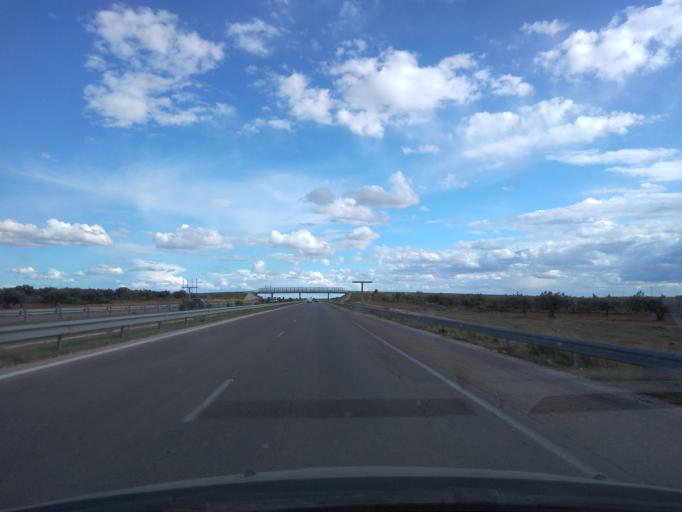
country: TN
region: Al Munastir
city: Manzil Kamil
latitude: 35.6369
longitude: 10.5825
